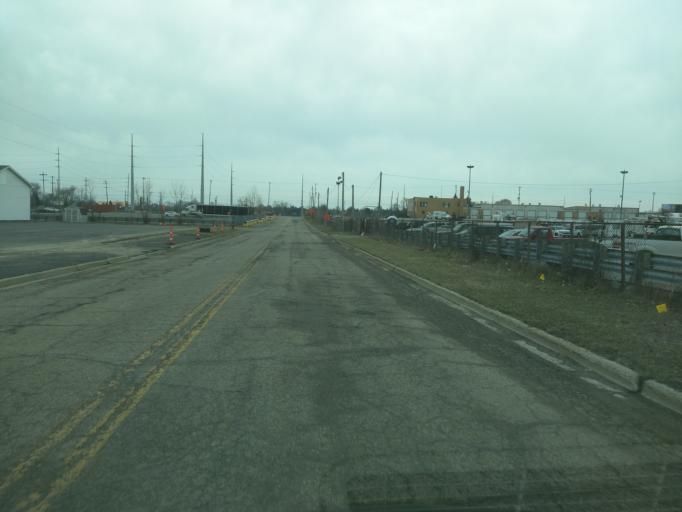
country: US
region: Michigan
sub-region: Ingham County
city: Edgemont Park
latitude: 42.7293
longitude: -84.5833
